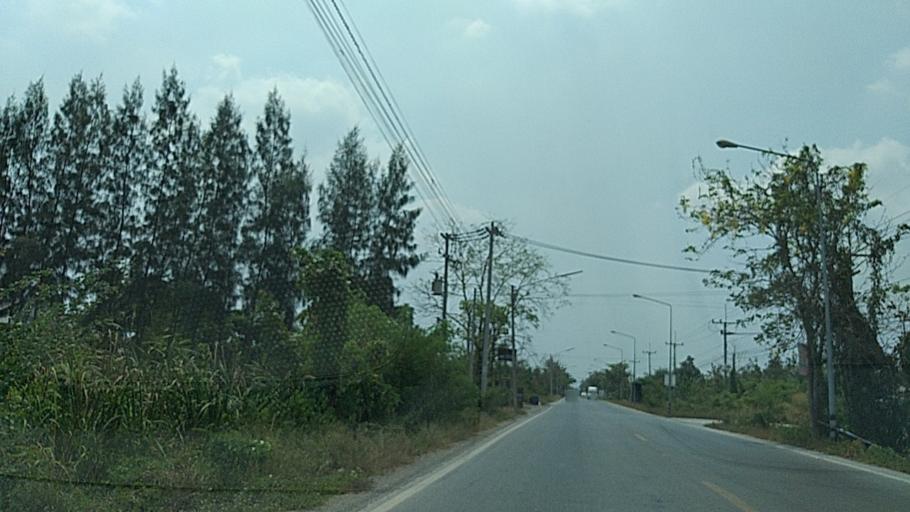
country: TH
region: Pathum Thani
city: Ban Lam Luk Ka
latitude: 13.9689
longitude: 100.8405
